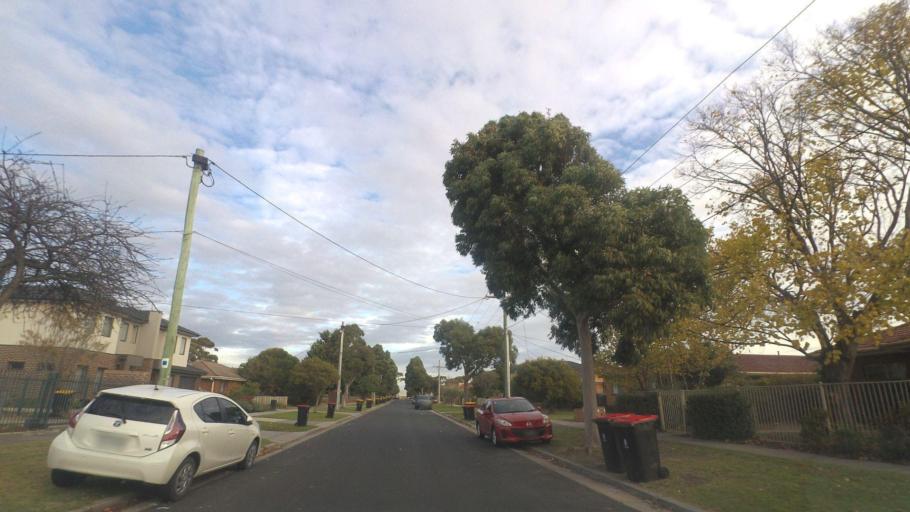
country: AU
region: Victoria
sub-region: Kingston
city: Clayton South
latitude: -37.9361
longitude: 145.1297
